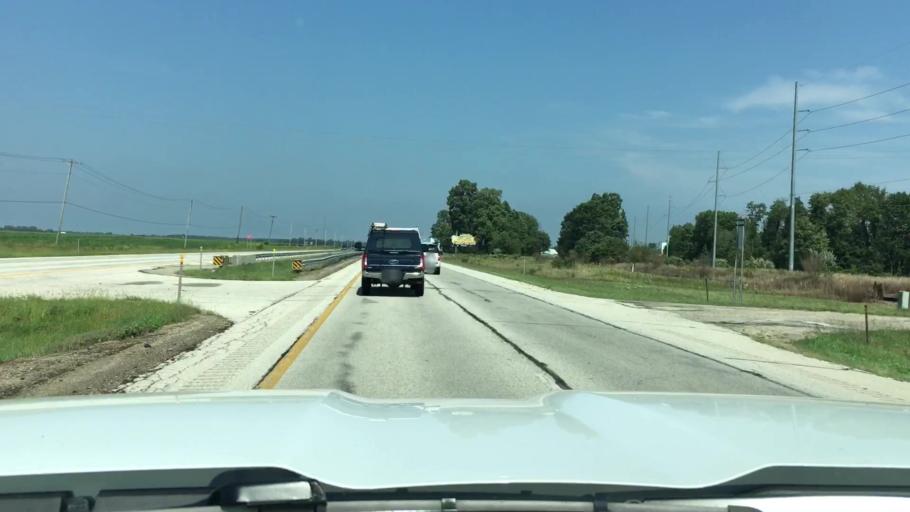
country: US
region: Michigan
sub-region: Kalamazoo County
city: Schoolcraft
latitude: 42.0675
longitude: -85.6363
